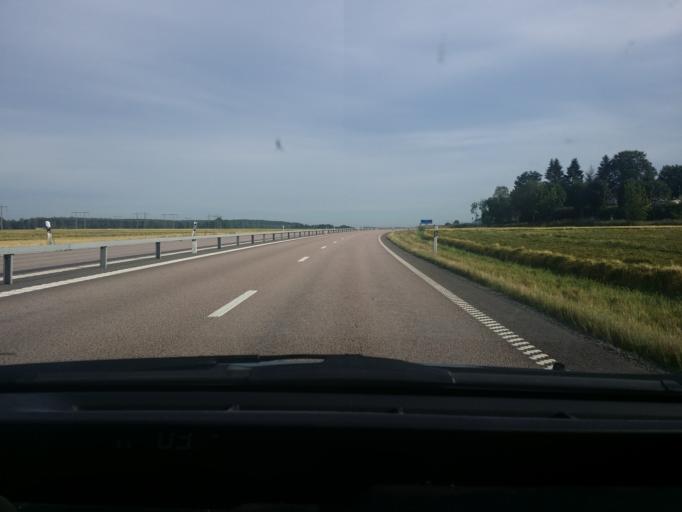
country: SE
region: Vaestmanland
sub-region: Vasteras
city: Hokasen
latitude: 59.7492
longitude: 16.5556
